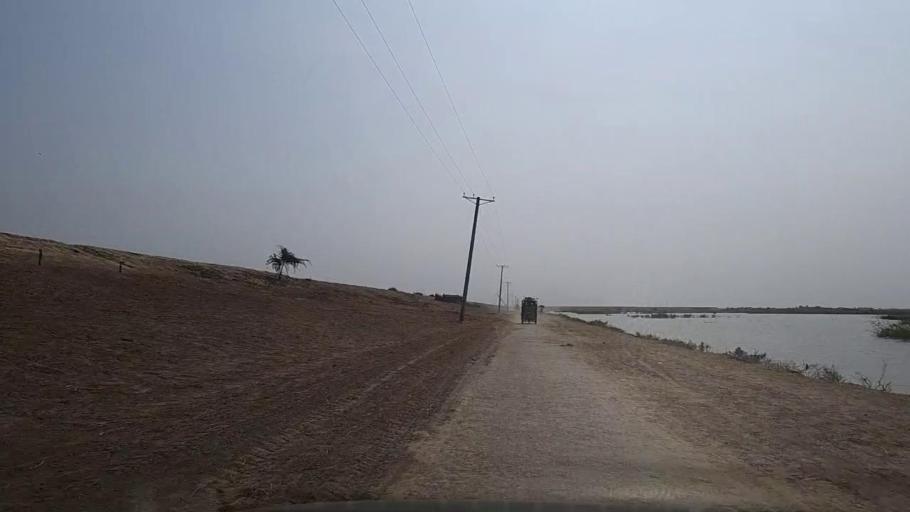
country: PK
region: Sindh
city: Thatta
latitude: 24.5812
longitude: 67.9150
